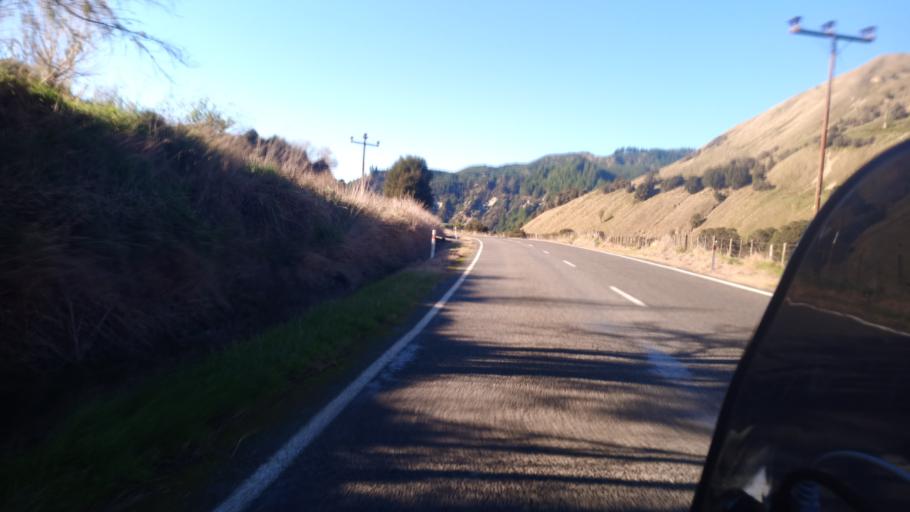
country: NZ
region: Hawke's Bay
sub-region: Wairoa District
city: Wairoa
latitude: -38.8753
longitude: 177.2192
